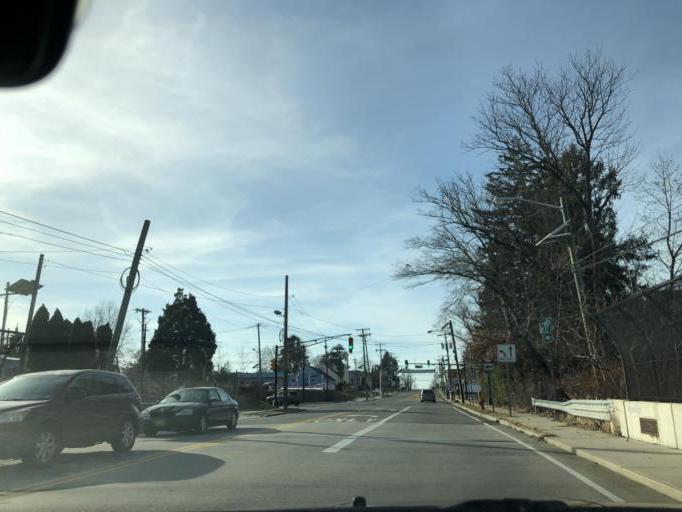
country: US
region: New Jersey
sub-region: Burlington County
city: Maple Shade
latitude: 39.9569
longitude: -74.9876
